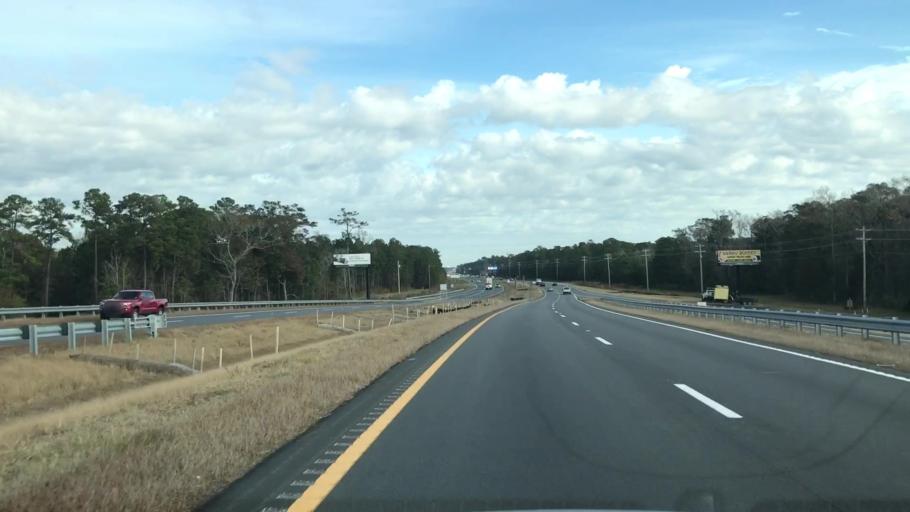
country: US
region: South Carolina
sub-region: Horry County
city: Garden City
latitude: 33.6227
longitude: -79.0033
